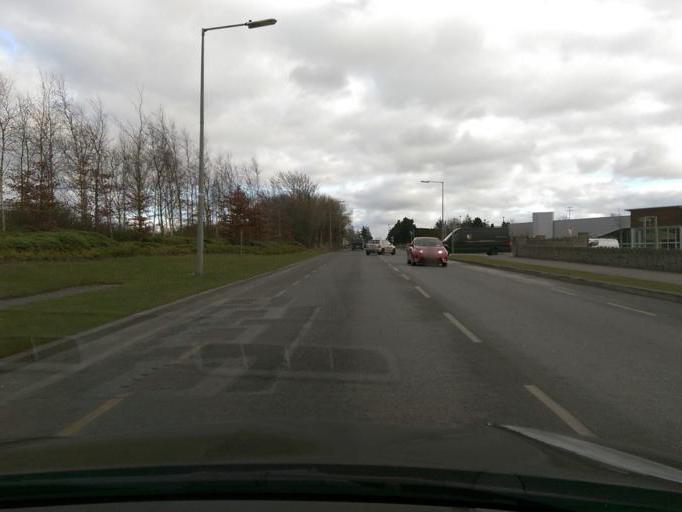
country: IE
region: Leinster
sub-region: An Iarmhi
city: Athlone
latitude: 53.4140
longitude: -7.8970
